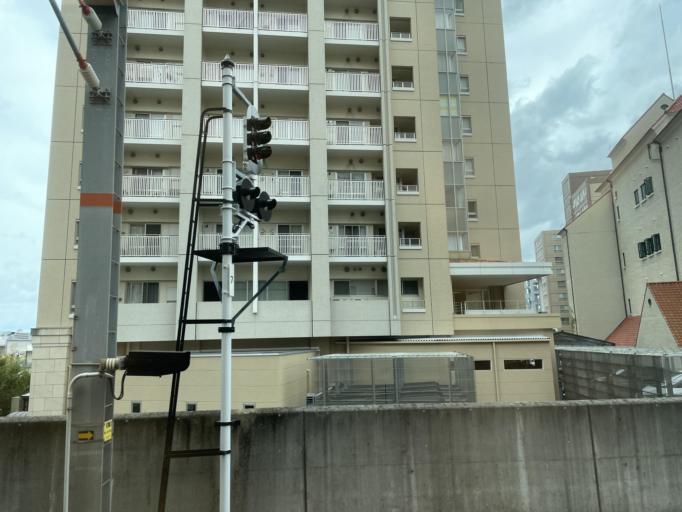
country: JP
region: Hyogo
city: Takarazuka
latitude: 34.8069
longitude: 135.3470
